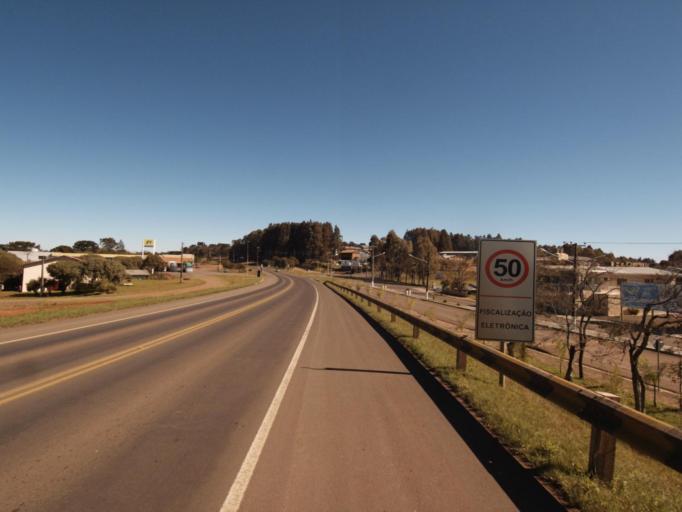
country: BR
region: Santa Catarina
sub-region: Xanxere
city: Xanxere
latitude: -26.8578
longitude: -52.2640
